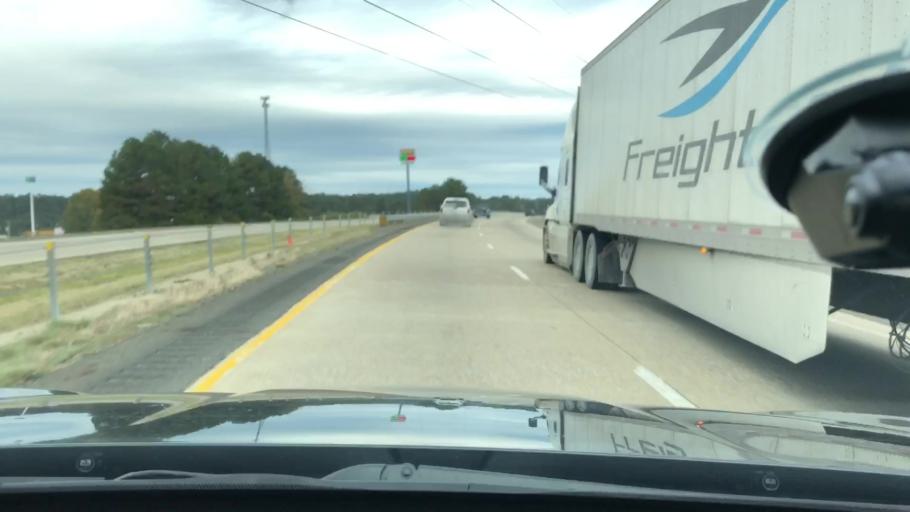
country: US
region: Arkansas
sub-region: Clark County
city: Arkadelphia
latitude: 34.1835
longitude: -93.0720
